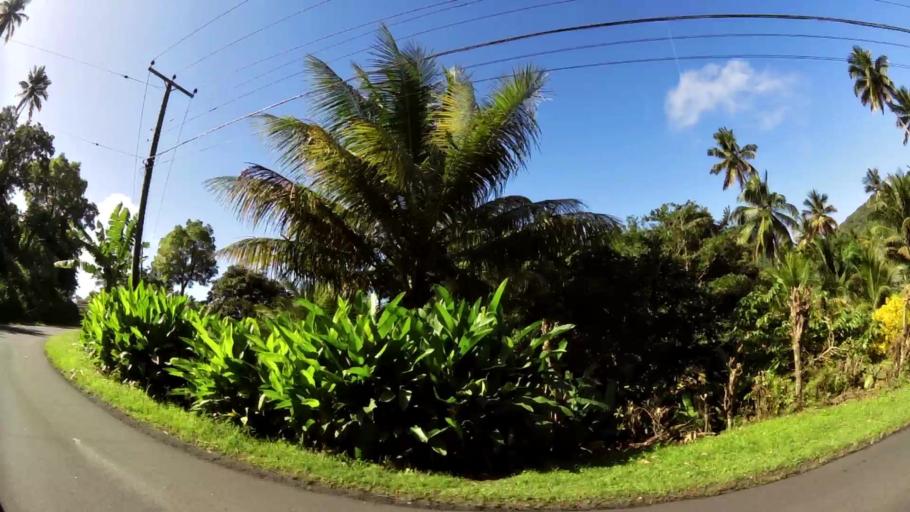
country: LC
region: Soufriere
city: Soufriere
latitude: 13.8206
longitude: -61.0442
